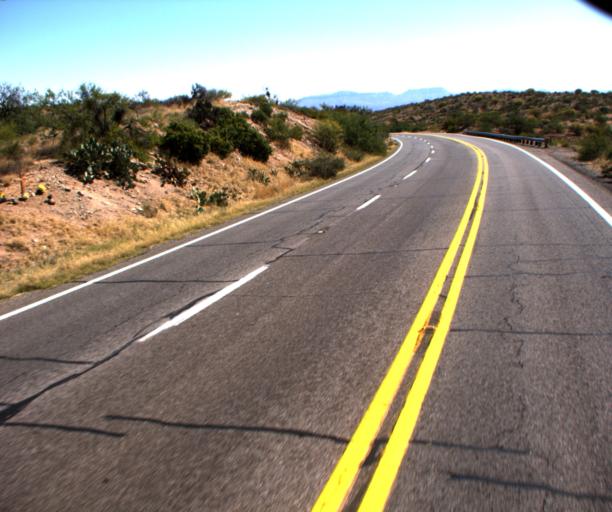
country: US
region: Arizona
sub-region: Pinal County
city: Oracle
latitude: 32.6521
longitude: -110.7045
